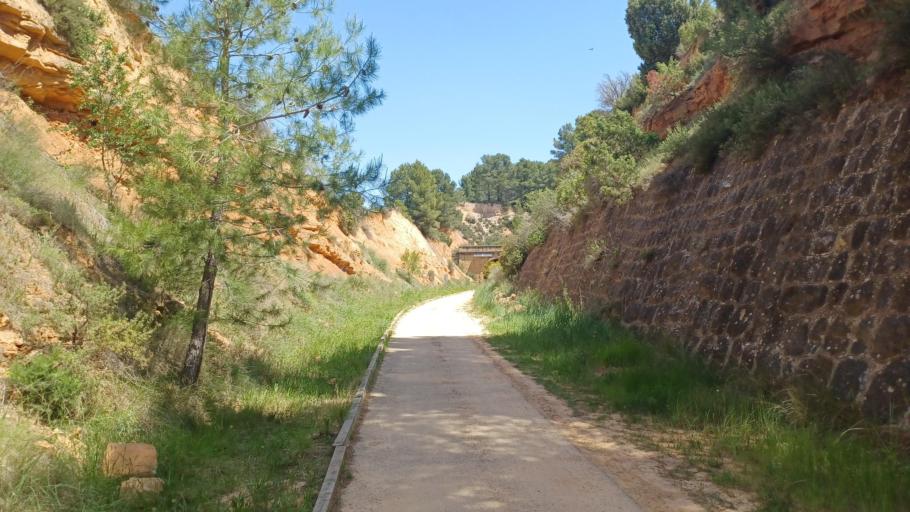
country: ES
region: Catalonia
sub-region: Provincia de Tarragona
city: Bot
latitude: 41.0095
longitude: 0.3933
